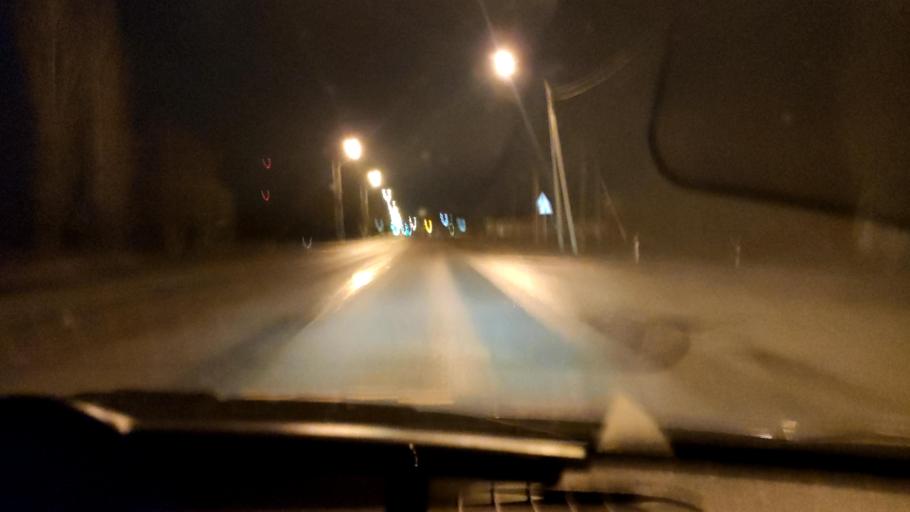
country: RU
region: Voronezj
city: Semiluki
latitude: 51.7058
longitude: 39.0208
